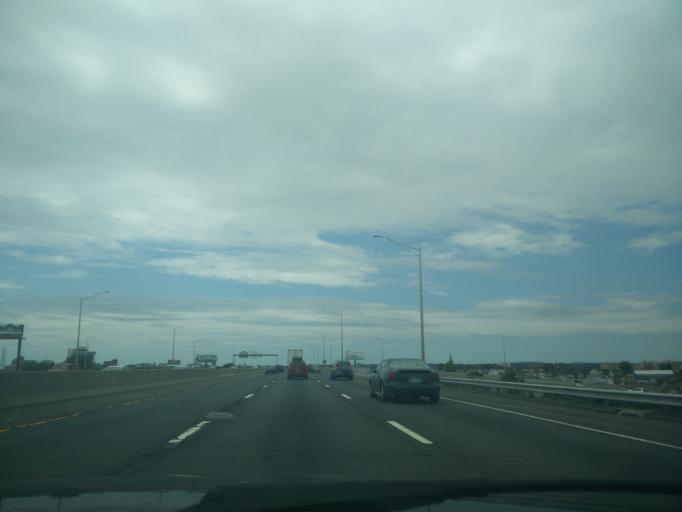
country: US
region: Connecticut
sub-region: Fairfield County
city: Bridgeport
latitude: 41.1768
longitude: -73.1719
